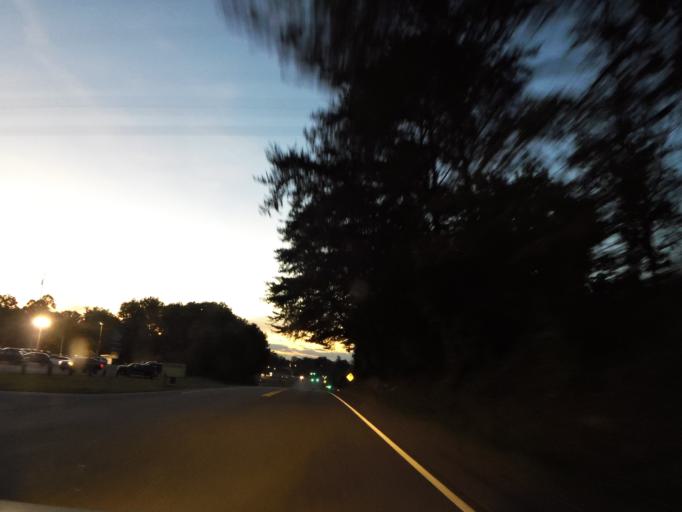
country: US
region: Tennessee
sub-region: Knox County
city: Mascot
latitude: 36.0249
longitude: -83.7239
